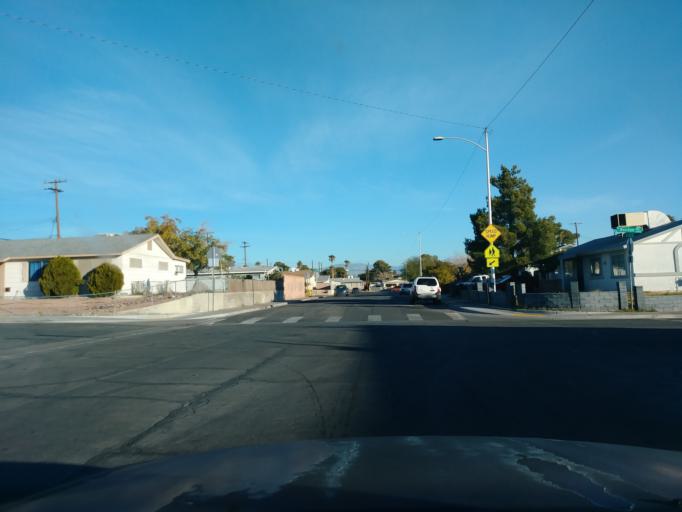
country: US
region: Nevada
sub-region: Clark County
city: Spring Valley
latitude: 36.1642
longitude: -115.2365
